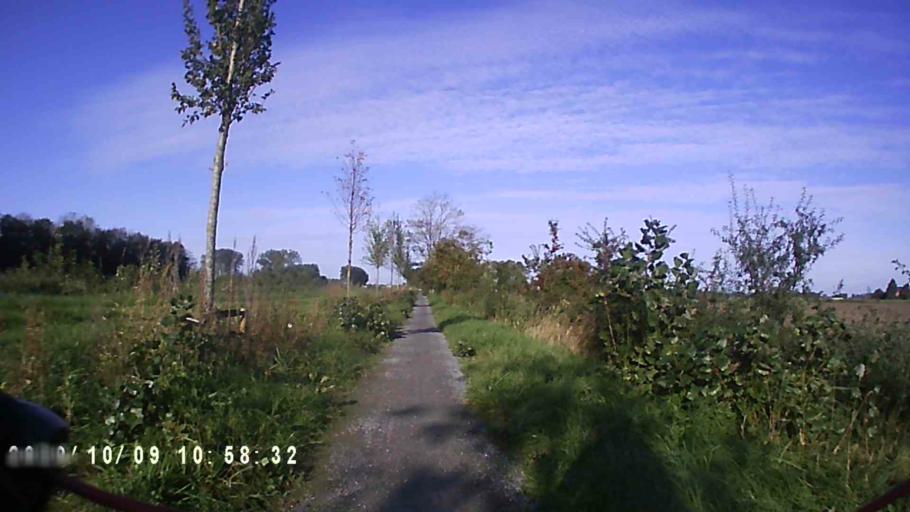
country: NL
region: Groningen
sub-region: Gemeente Groningen
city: Korrewegwijk
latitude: 53.2549
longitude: 6.5169
